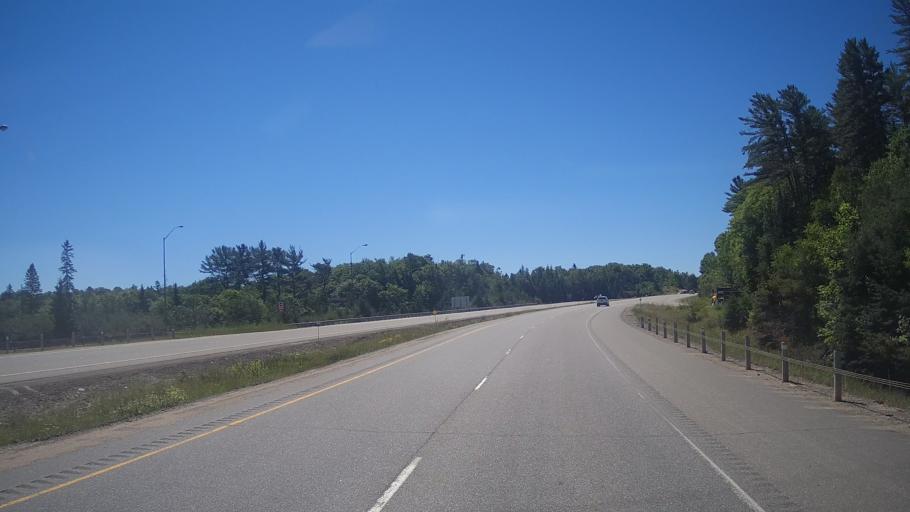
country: CA
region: Ontario
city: Bracebridge
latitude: 45.0844
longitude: -79.2977
